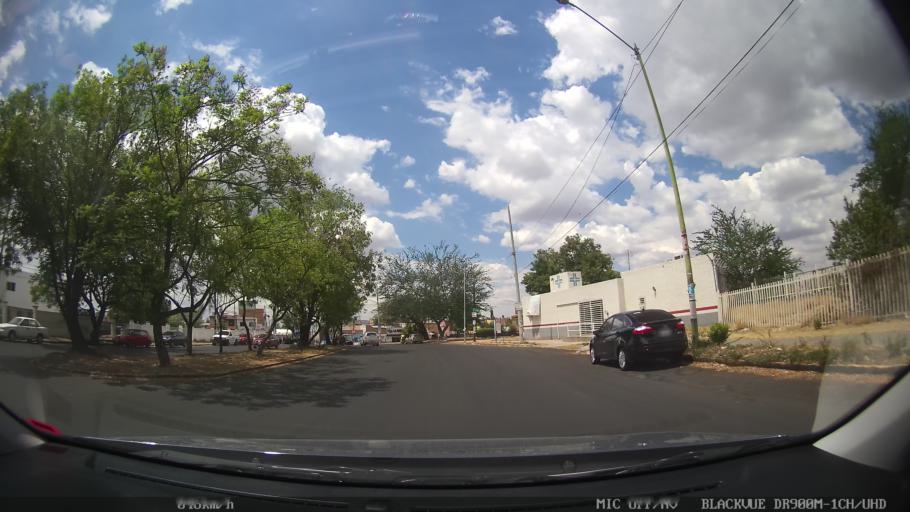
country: MX
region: Jalisco
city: Tlaquepaque
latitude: 20.6471
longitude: -103.2801
